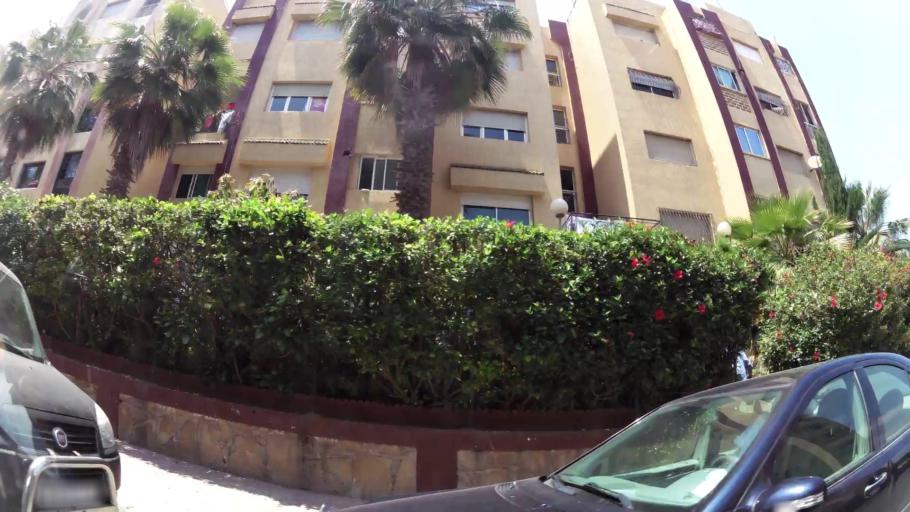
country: MA
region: Rabat-Sale-Zemmour-Zaer
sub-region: Skhirate-Temara
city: Temara
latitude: 33.9746
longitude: -6.8939
